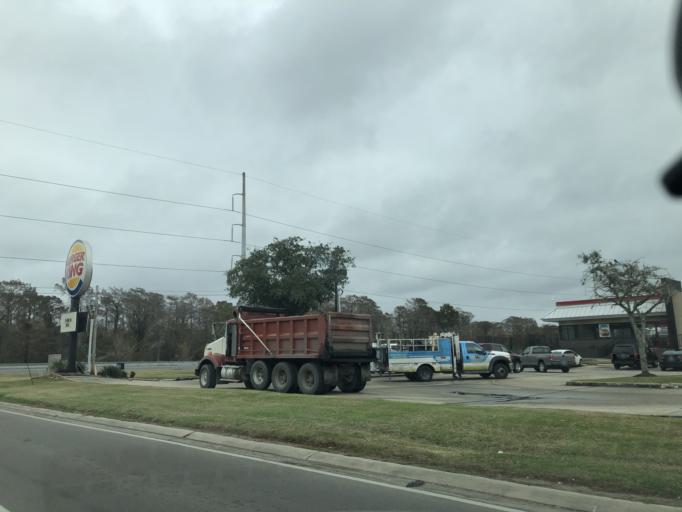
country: US
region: Louisiana
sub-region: Saint Charles Parish
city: New Sarpy
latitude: 29.9869
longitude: -90.3634
